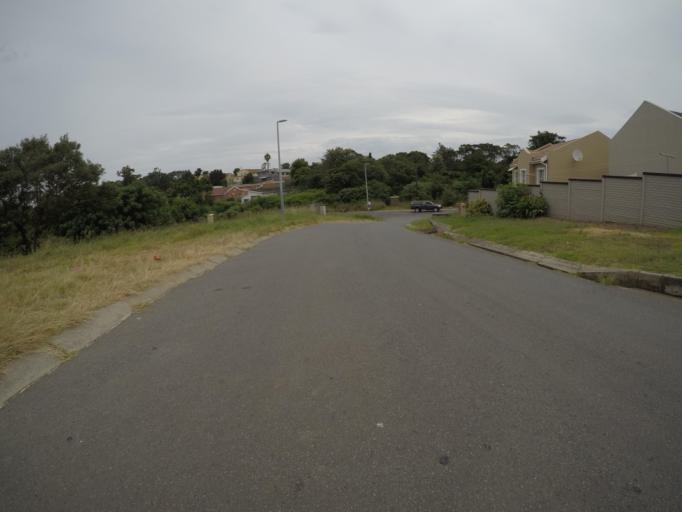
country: ZA
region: Eastern Cape
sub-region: Buffalo City Metropolitan Municipality
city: East London
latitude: -32.9967
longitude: 27.8504
